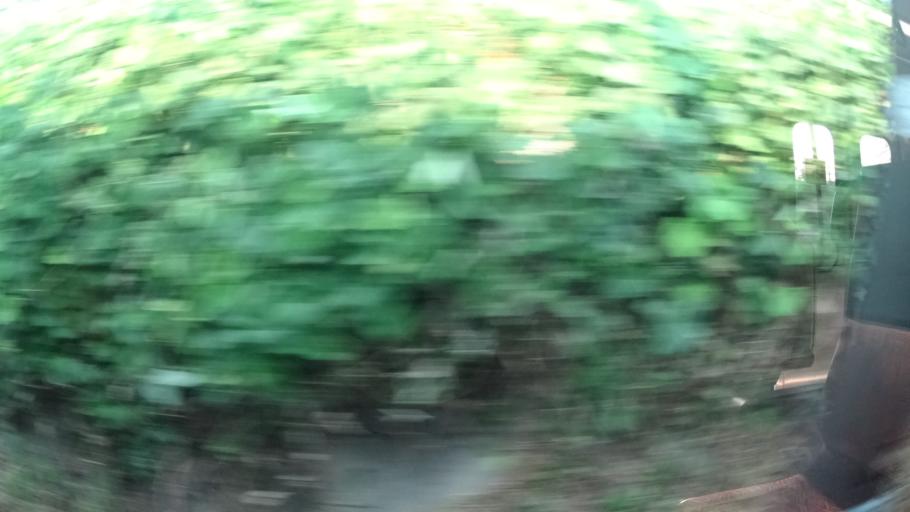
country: JP
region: Ibaraki
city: Hitachi
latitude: 36.6442
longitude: 140.6736
